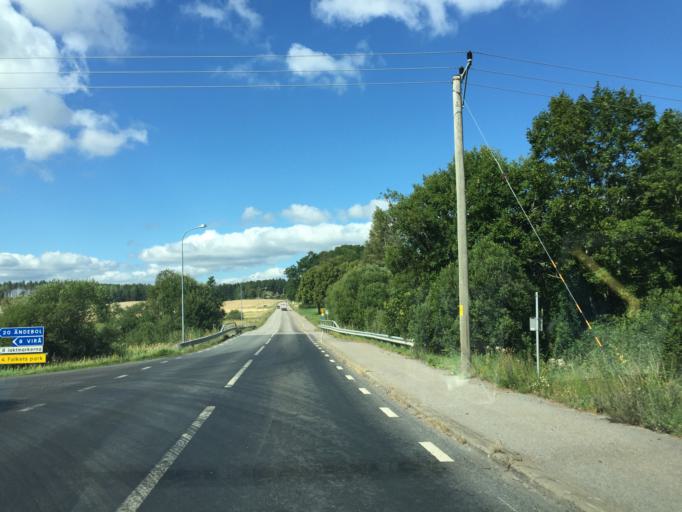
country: SE
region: Soedermanland
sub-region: Nykopings Kommun
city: Olstorp
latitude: 58.8288
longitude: 16.5209
